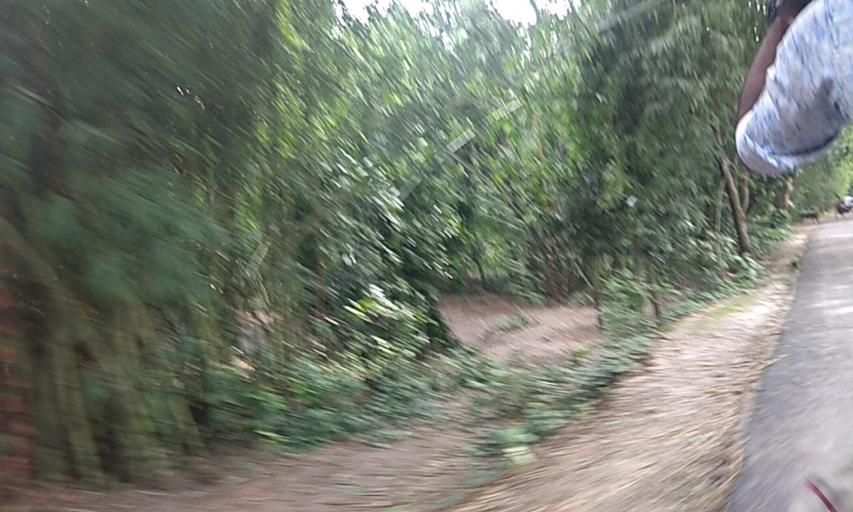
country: BD
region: Dhaka
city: Dohar
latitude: 23.4747
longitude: 90.0475
